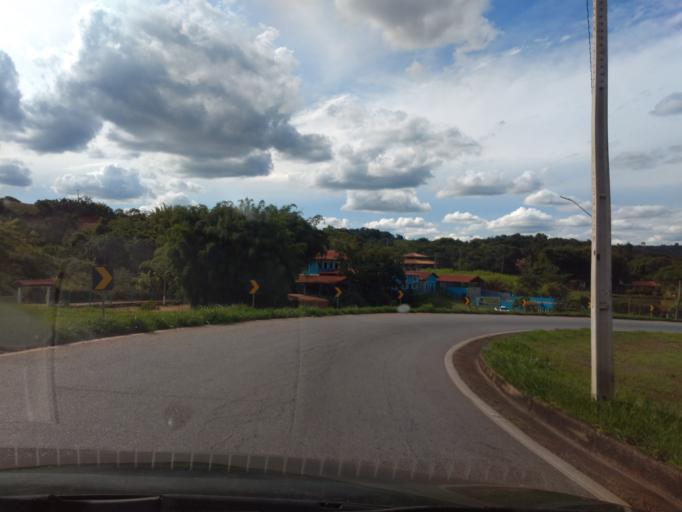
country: BR
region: Minas Gerais
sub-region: Tres Coracoes
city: Tres Coracoes
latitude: -21.6561
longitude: -45.3025
